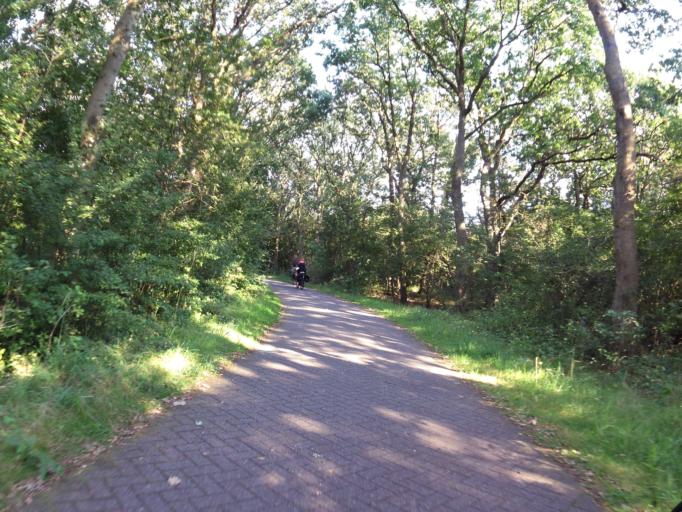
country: NL
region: North Holland
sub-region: Gemeente Castricum
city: Castricum
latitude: 52.5507
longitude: 4.6457
